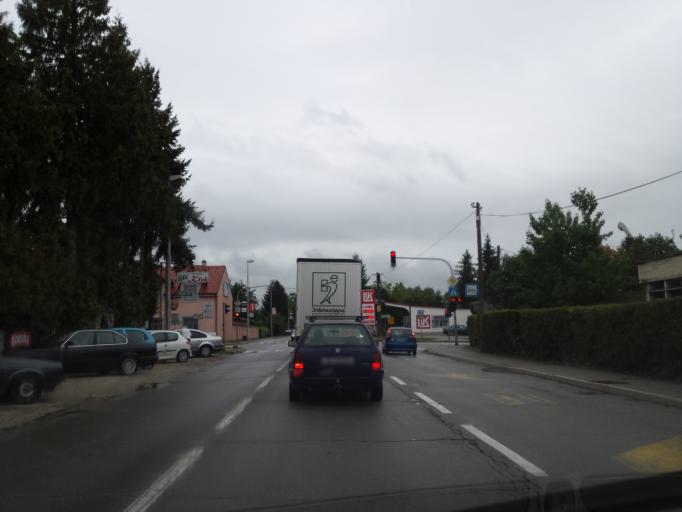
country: HR
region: Zagrebacka
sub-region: Grad Samobor
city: Samobor
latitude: 45.8042
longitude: 15.7202
